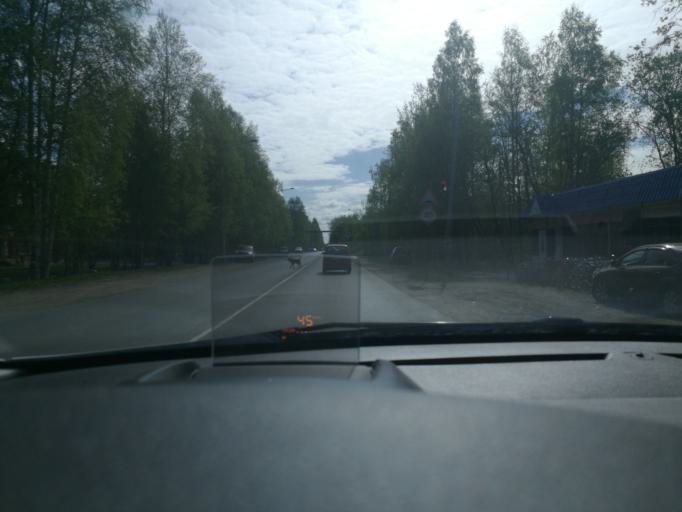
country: RU
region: Arkhangelskaya
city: Arkhangel'sk
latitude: 64.5934
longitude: 40.5849
